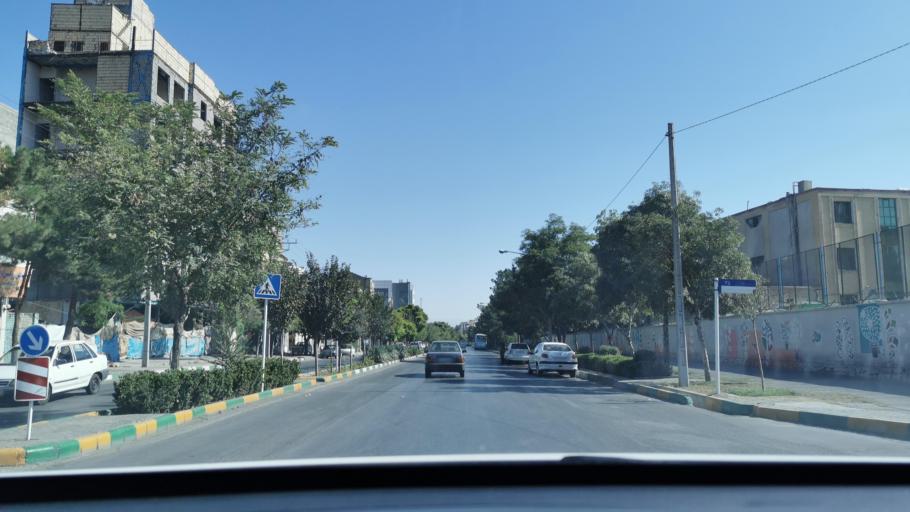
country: IR
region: Razavi Khorasan
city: Mashhad
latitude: 36.3333
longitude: 59.5919
